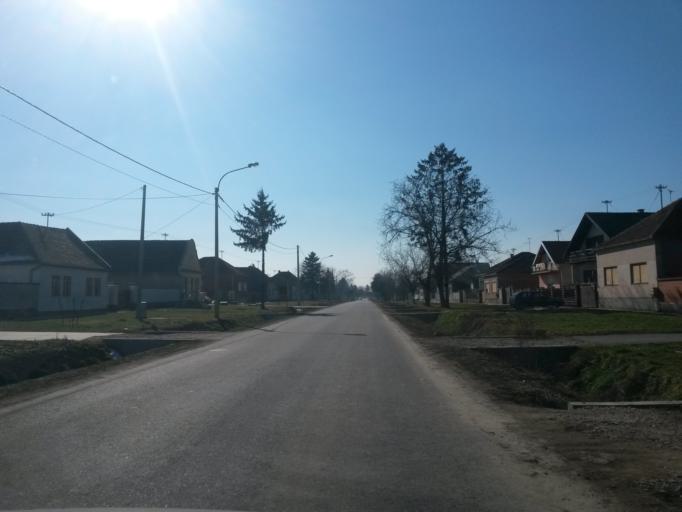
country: HR
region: Vukovarsko-Srijemska
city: Negoslavci
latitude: 45.2831
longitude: 18.9985
